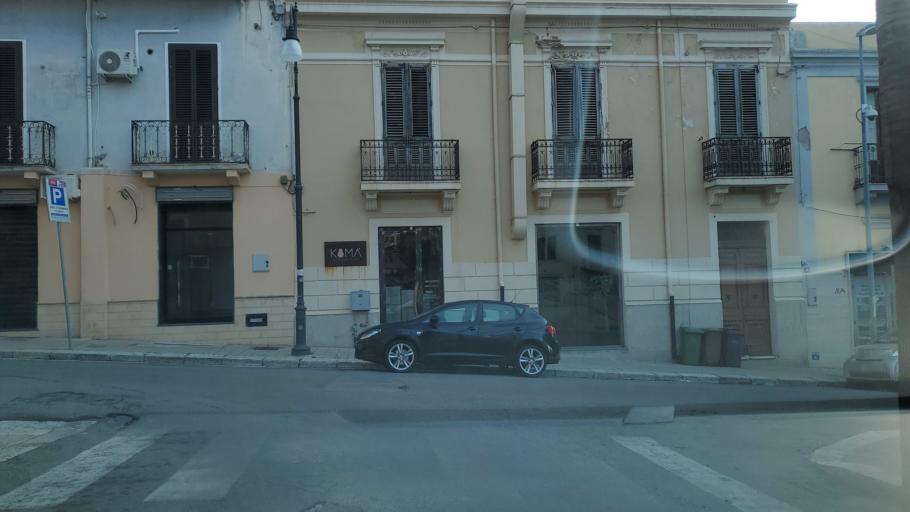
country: IT
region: Calabria
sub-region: Provincia di Reggio Calabria
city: Reggio Calabria
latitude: 38.1070
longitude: 15.6463
